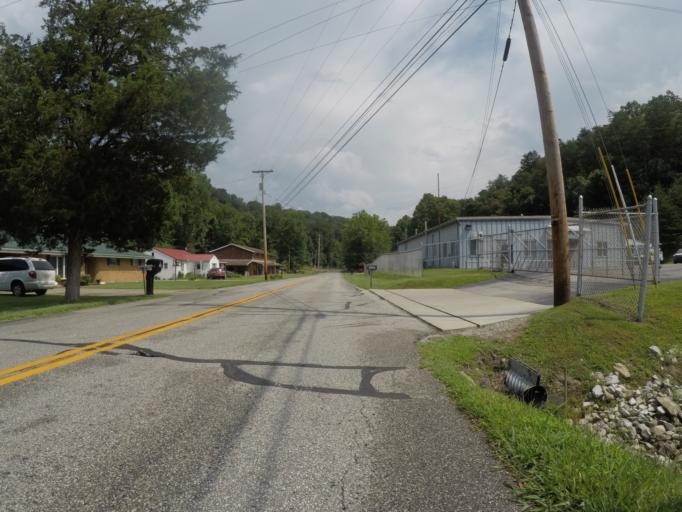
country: US
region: Kentucky
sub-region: Boyd County
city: Ironville
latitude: 38.4496
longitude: -82.6871
